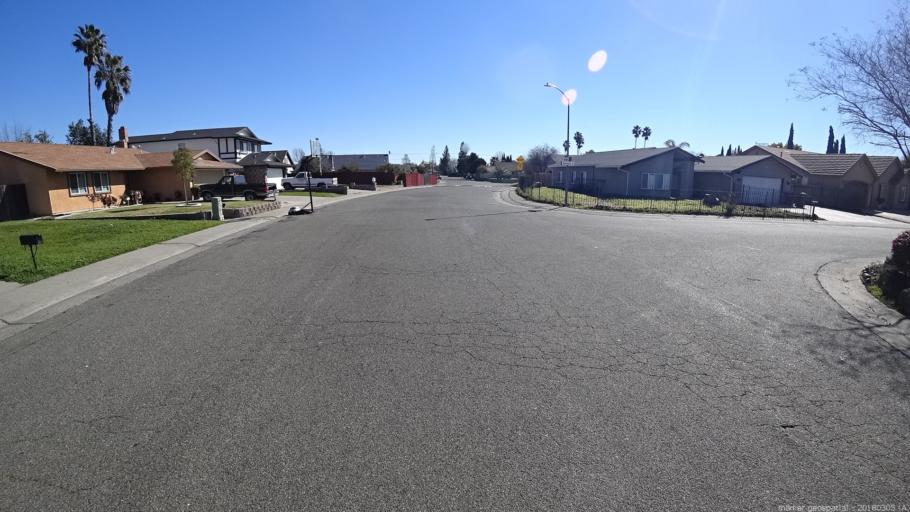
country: US
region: California
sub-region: Sacramento County
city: Florin
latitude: 38.4836
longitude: -121.4118
